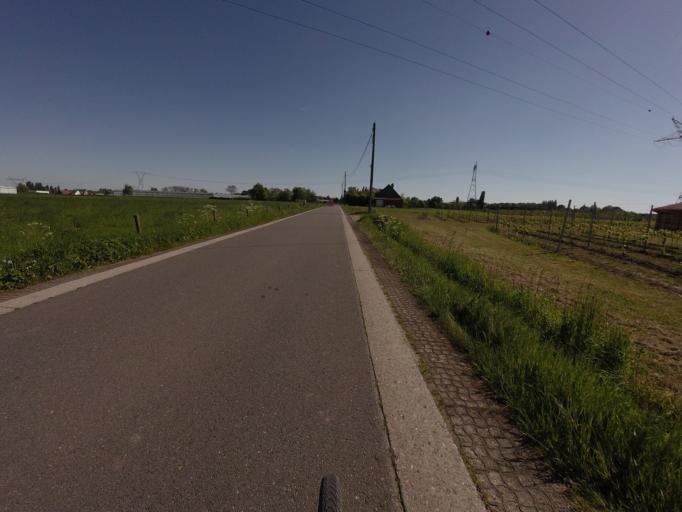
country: BE
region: Flanders
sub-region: Provincie Antwerpen
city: Boechout
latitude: 51.1761
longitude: 4.5001
